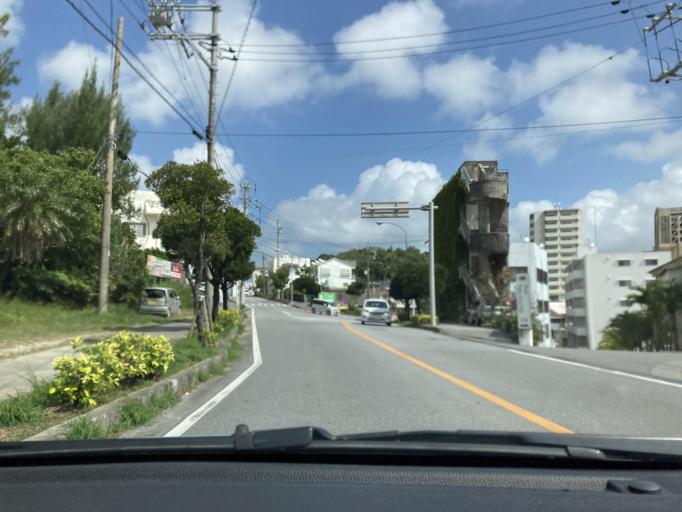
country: JP
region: Okinawa
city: Okinawa
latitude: 26.3201
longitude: 127.8079
